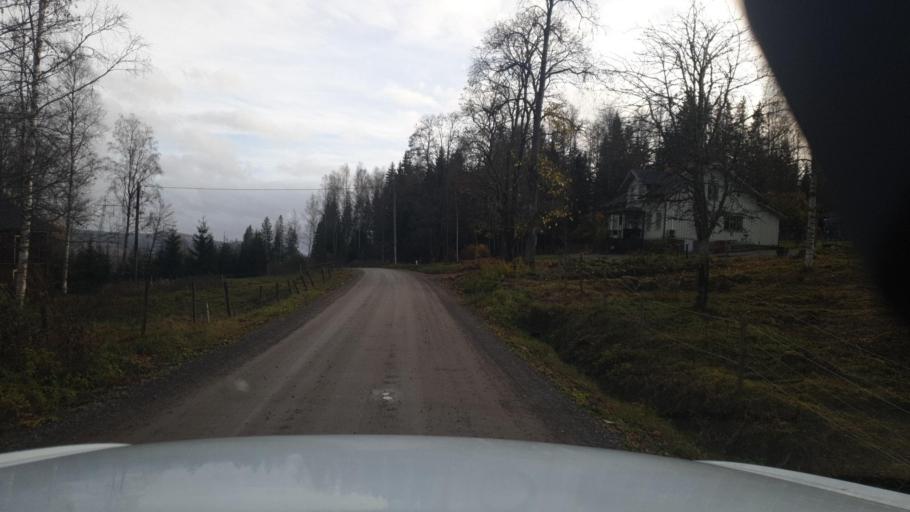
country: SE
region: Vaermland
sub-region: Torsby Kommun
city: Torsby
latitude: 59.9593
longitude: 12.8868
